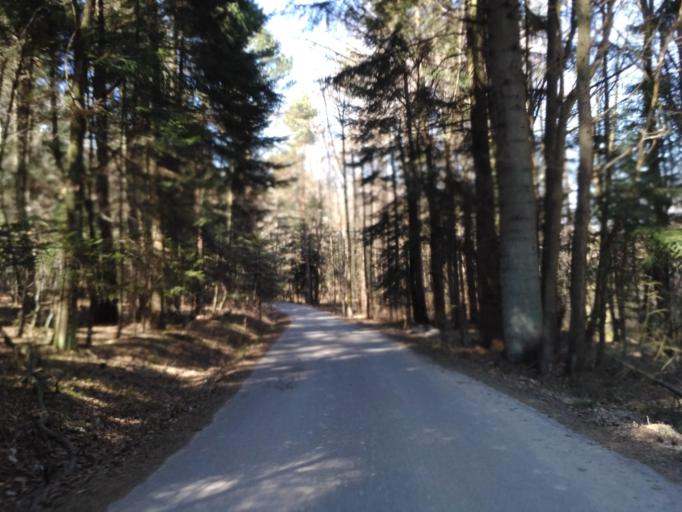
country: PL
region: Subcarpathian Voivodeship
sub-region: Powiat brzozowski
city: Zmiennica
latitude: 49.7061
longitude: 21.9686
